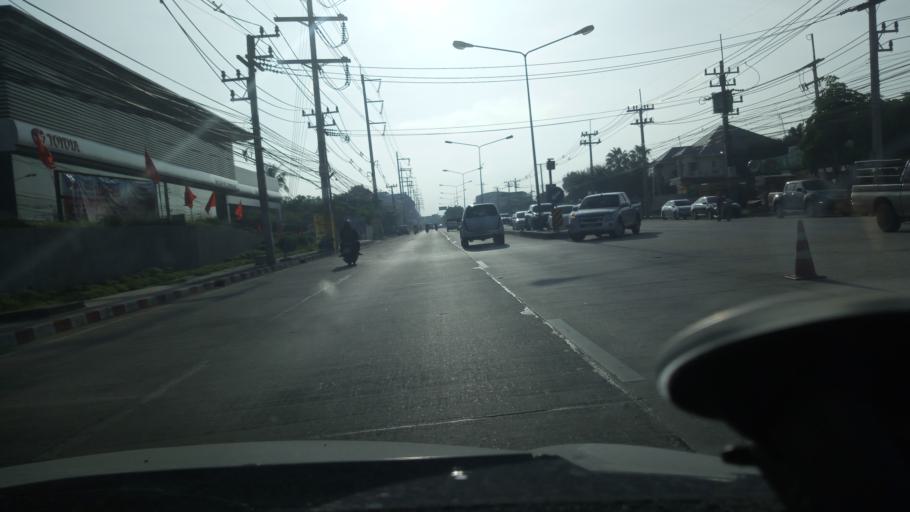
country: TH
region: Chon Buri
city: Phan Thong
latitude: 13.4224
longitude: 101.1028
